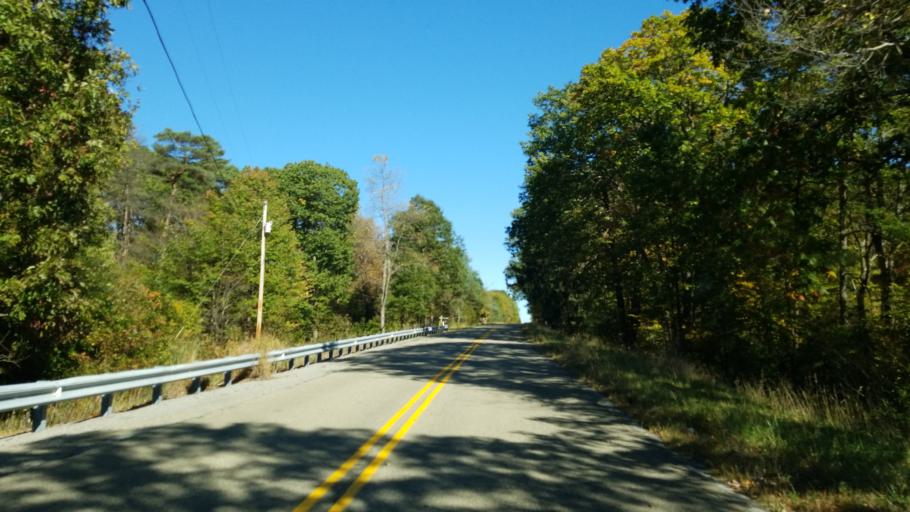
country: US
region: Pennsylvania
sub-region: Clearfield County
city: Shiloh
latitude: 41.2552
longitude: -78.3283
